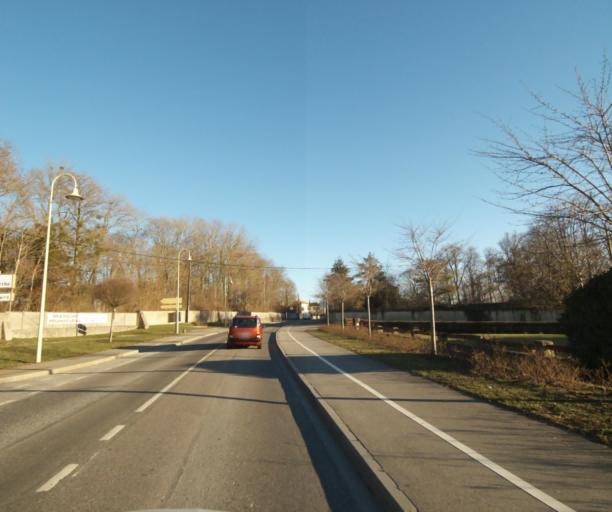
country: FR
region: Lorraine
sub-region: Departement de Meurthe-et-Moselle
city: Art-sur-Meurthe
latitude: 48.6576
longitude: 6.2625
